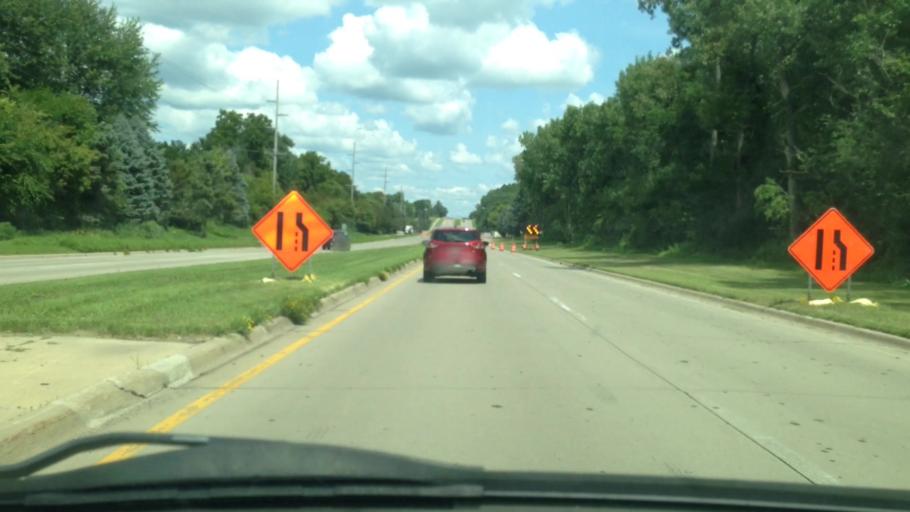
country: US
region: Minnesota
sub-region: Olmsted County
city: Rochester
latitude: 44.0227
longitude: -92.5162
